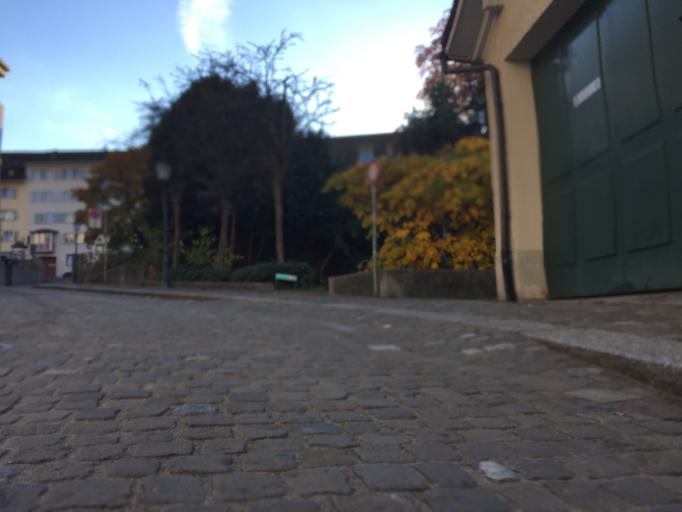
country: CH
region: Zurich
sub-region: Bezirk Zuerich
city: Zuerich (Kreis 1) / Rathaus
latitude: 47.3722
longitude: 8.5464
